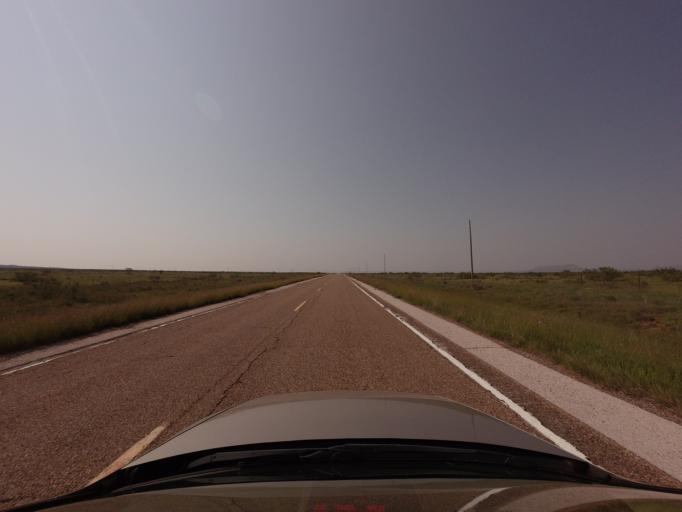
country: US
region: New Mexico
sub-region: Quay County
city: Tucumcari
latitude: 35.0025
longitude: -103.7432
